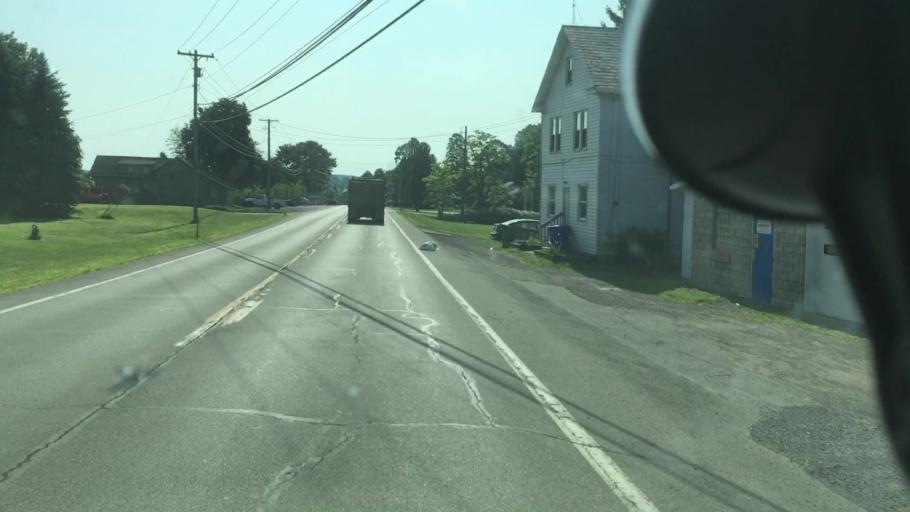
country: US
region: Pennsylvania
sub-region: Lawrence County
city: New Castle
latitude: 41.0131
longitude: -80.2569
